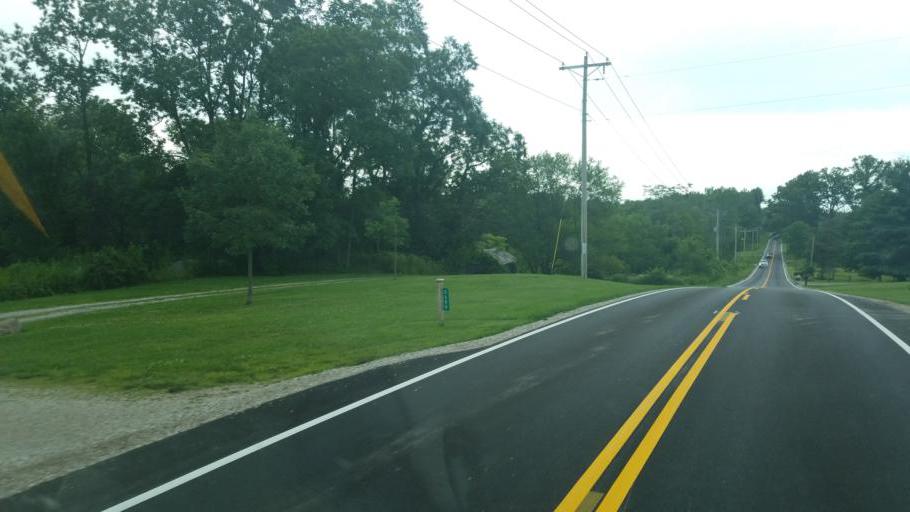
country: US
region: Ohio
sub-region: Delaware County
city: Ashley
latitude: 40.3413
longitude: -82.9195
